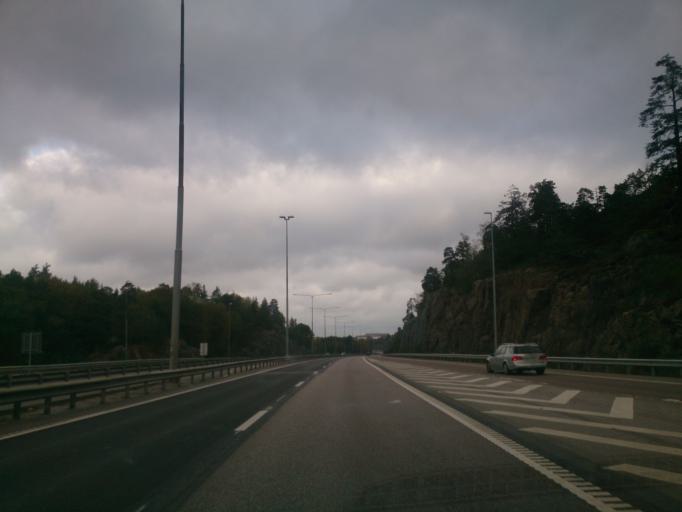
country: SE
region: Stockholm
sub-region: Haninge Kommun
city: Handen
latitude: 59.2312
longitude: 18.1243
